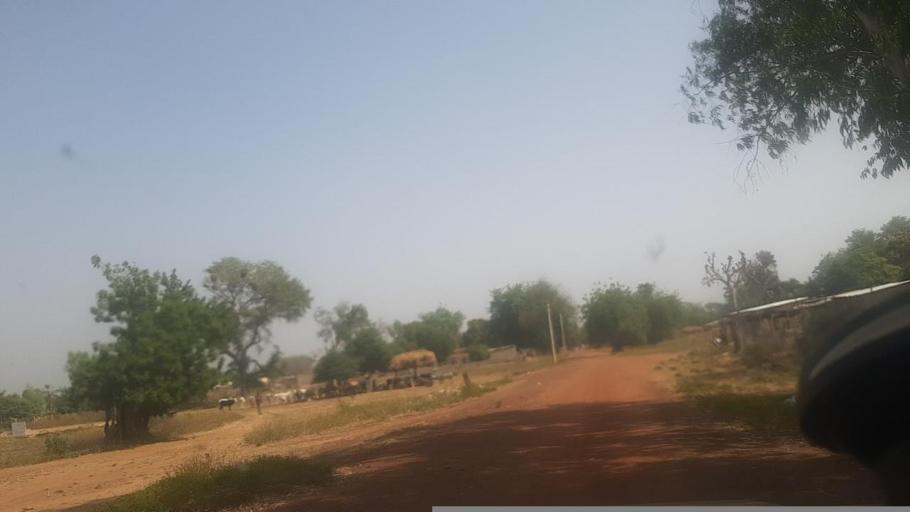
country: ML
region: Segou
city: Bla
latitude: 12.9124
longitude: -6.2448
